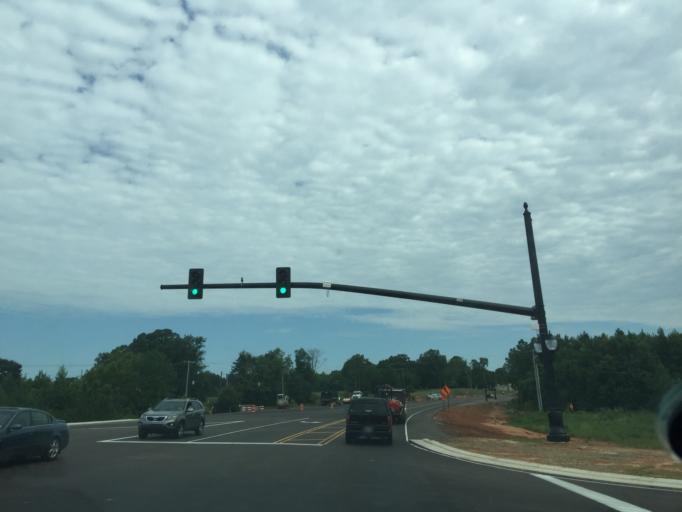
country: US
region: Mississippi
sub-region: Rankin County
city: Brandon
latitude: 32.2931
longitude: -89.9965
